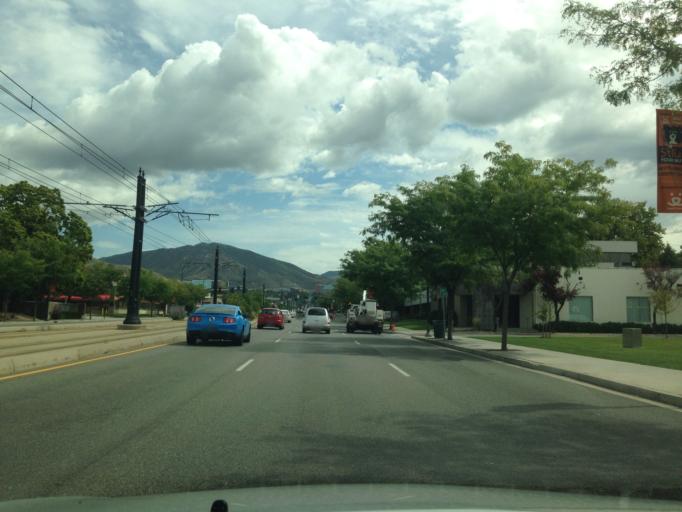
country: US
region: Utah
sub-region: Salt Lake County
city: Salt Lake City
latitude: 40.7606
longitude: -111.8818
